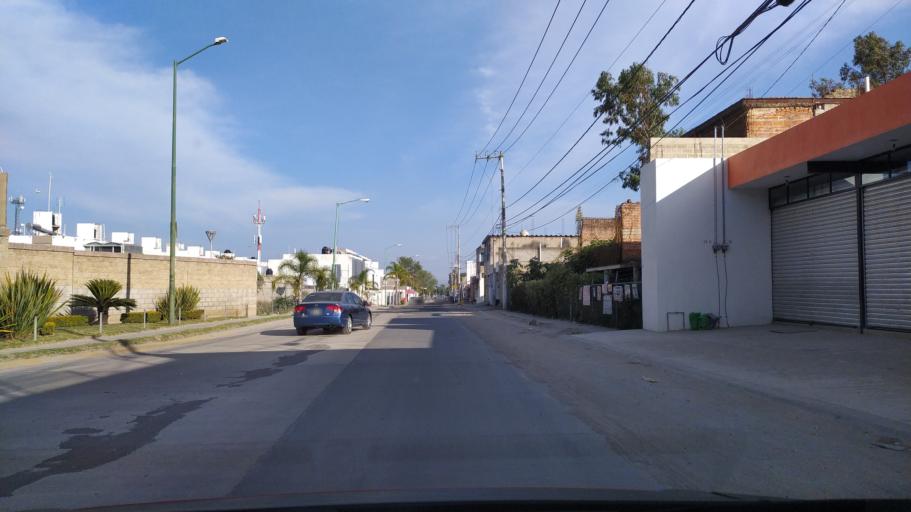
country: MX
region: Jalisco
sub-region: Tlajomulco de Zuniga
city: Palomar
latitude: 20.6270
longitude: -103.4807
